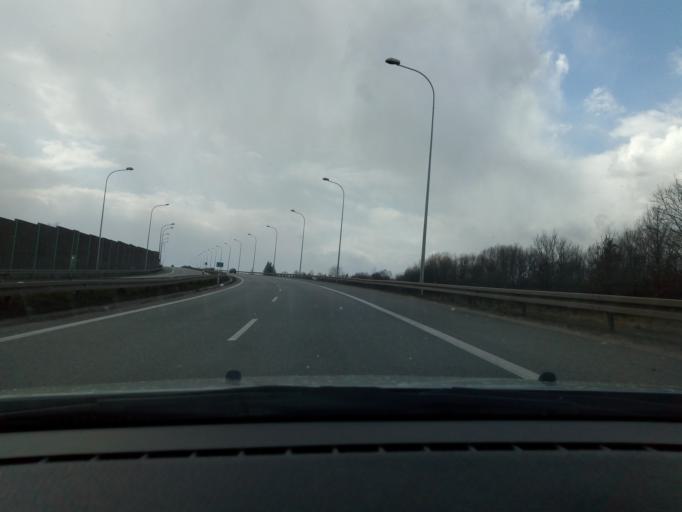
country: PL
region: Swietokrzyskie
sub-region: Powiat skarzyski
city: Skarzysko-Kamienna
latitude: 51.1074
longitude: 20.8416
